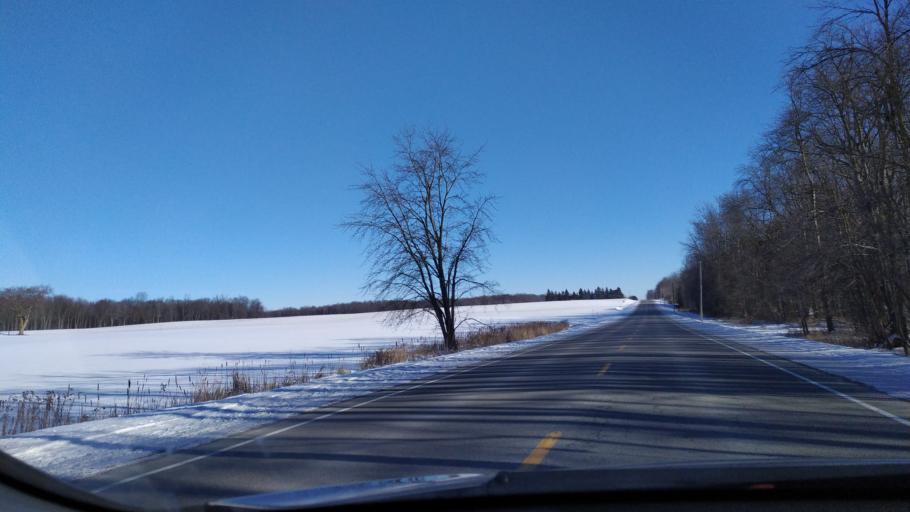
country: CA
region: Ontario
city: Stratford
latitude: 43.4239
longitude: -80.7756
